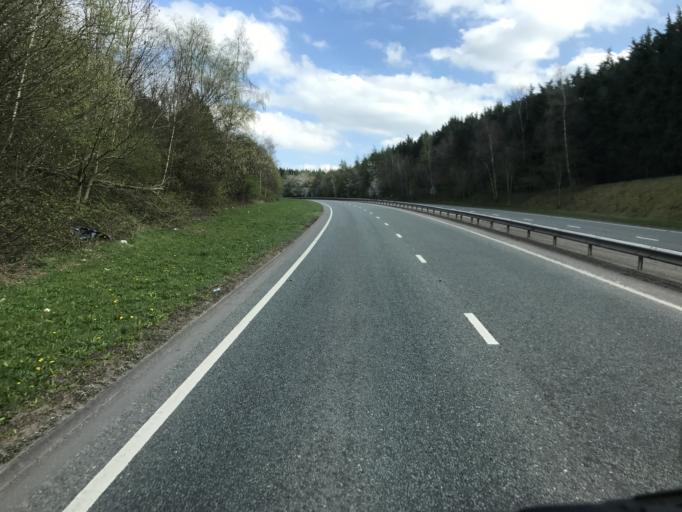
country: GB
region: England
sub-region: Cheshire West and Chester
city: Kelsall
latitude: 53.2133
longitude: -2.7149
